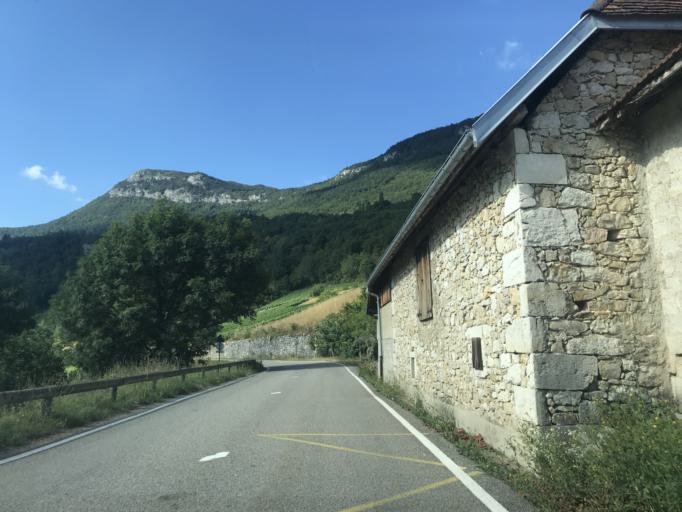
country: FR
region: Rhone-Alpes
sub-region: Departement de la Savoie
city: Brison-Saint-Innocent
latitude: 45.7093
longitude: 5.8289
